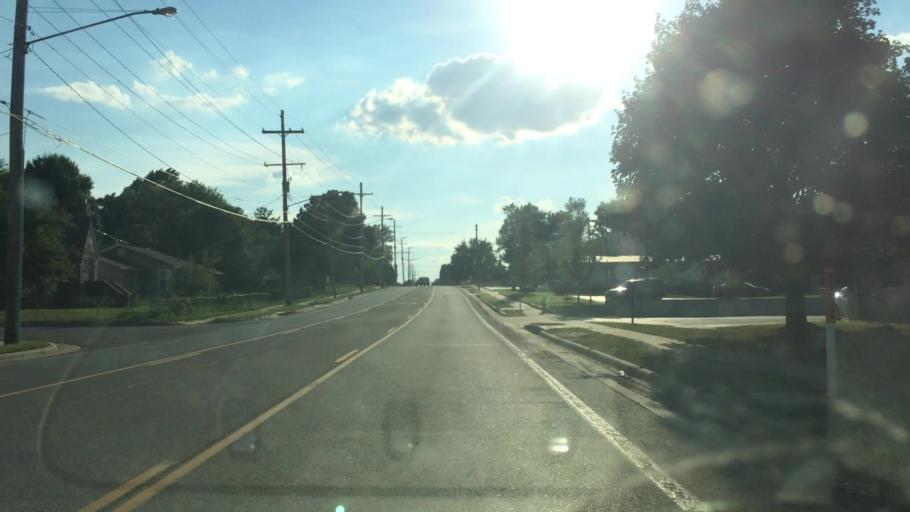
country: US
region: Missouri
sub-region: Greene County
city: Springfield
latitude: 37.2035
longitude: -93.2572
